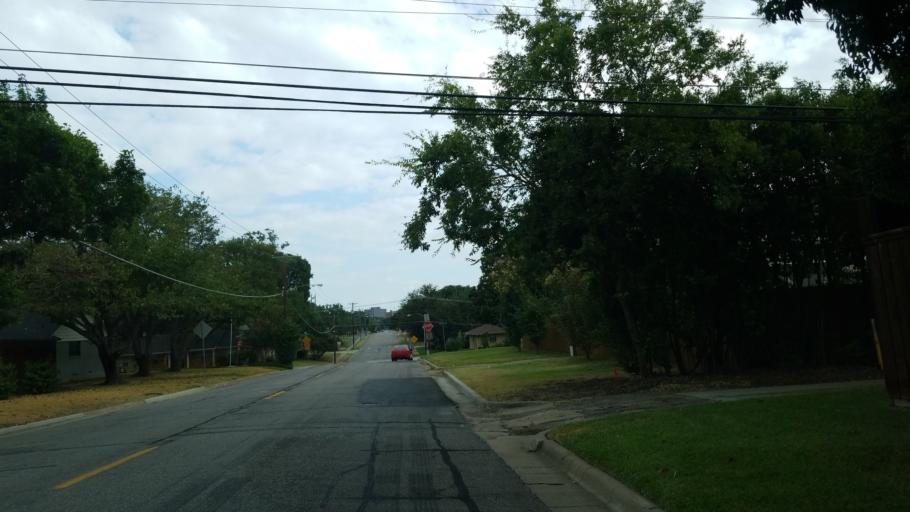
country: US
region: Texas
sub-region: Dallas County
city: Richardson
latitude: 32.9354
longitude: -96.7785
